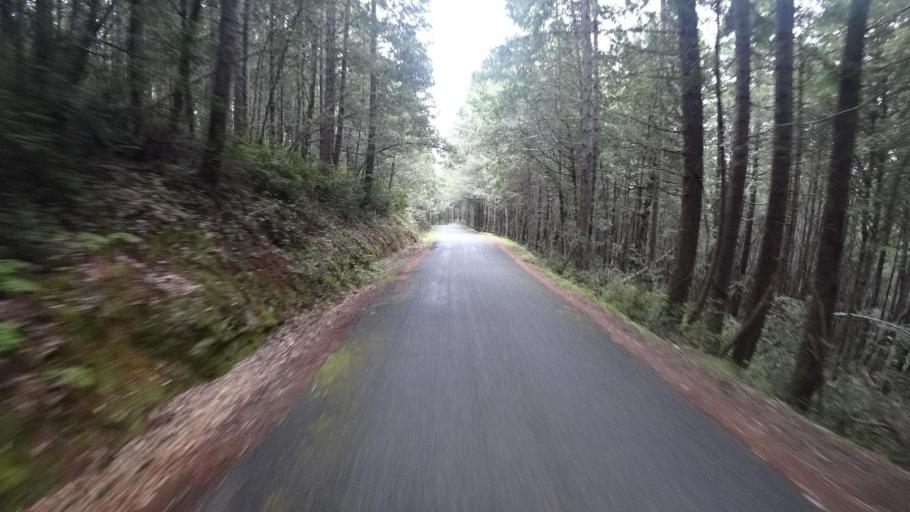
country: US
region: California
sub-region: Humboldt County
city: Willow Creek
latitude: 41.1986
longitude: -123.7677
